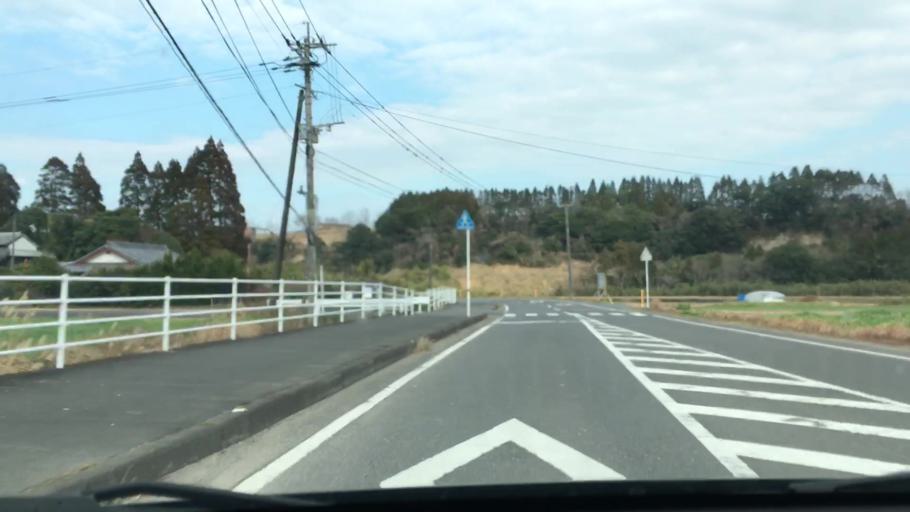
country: JP
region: Miyazaki
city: Kushima
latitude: 31.4966
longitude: 131.2381
